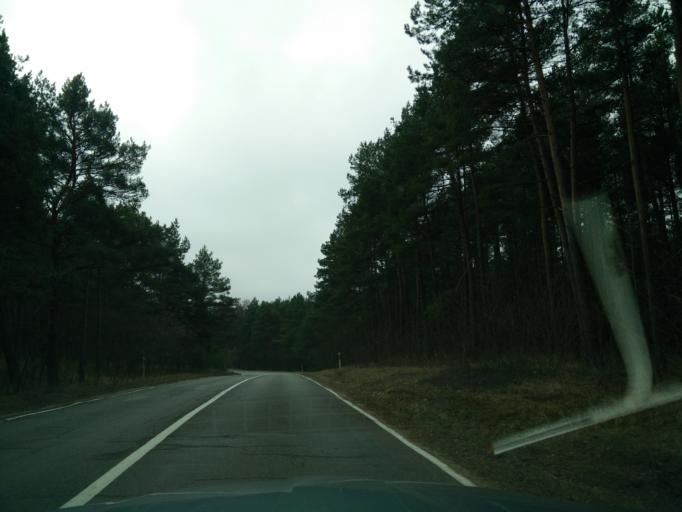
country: LT
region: Klaipedos apskritis
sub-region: Klaipeda
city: Klaipeda
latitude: 55.6633
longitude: 21.1163
